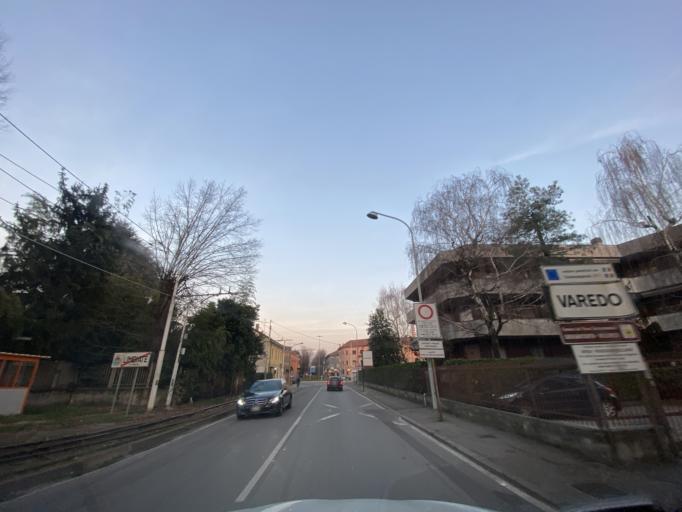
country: IT
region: Lombardy
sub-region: Provincia di Monza e Brianza
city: Bovisio-Masciago
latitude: 45.5970
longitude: 9.1445
